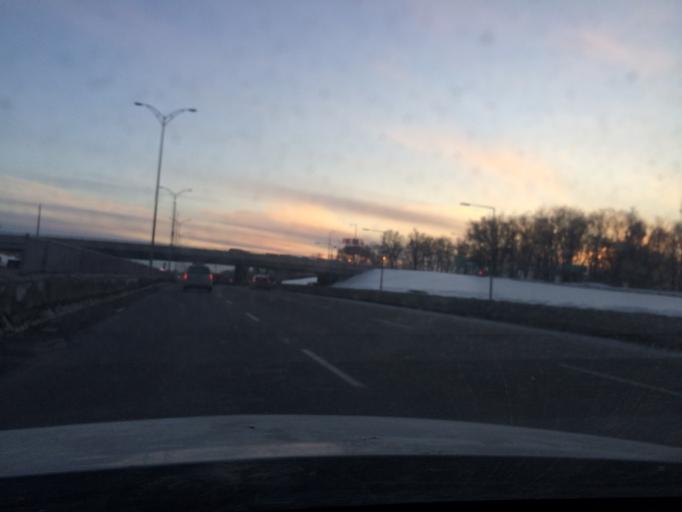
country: CA
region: Quebec
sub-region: Montreal
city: Saint-Leonard
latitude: 45.5837
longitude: -73.5878
